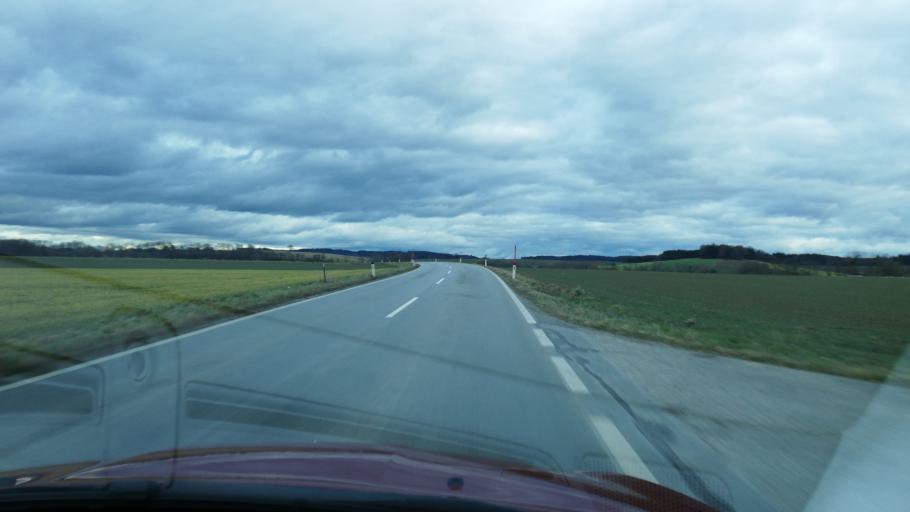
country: DE
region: Bavaria
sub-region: Lower Bavaria
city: Bad Fussing
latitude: 48.2657
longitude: 13.3228
